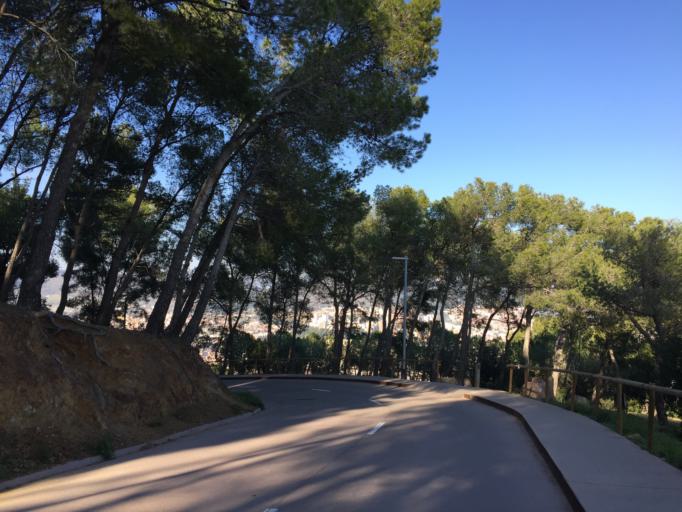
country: ES
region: Catalonia
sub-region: Provincia de Barcelona
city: Horta-Guinardo
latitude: 41.4198
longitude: 2.1662
